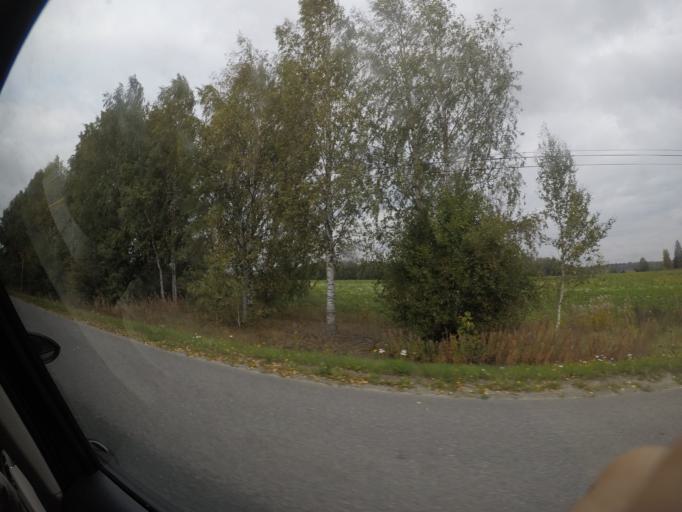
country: FI
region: Haeme
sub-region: Haemeenlinna
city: Haemeenlinna
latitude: 61.0303
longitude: 24.4181
